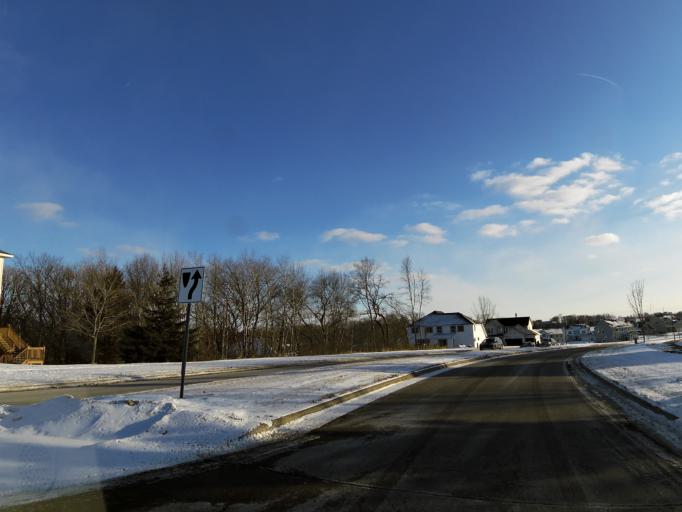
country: US
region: Minnesota
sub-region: Scott County
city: Prior Lake
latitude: 44.7110
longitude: -93.4076
